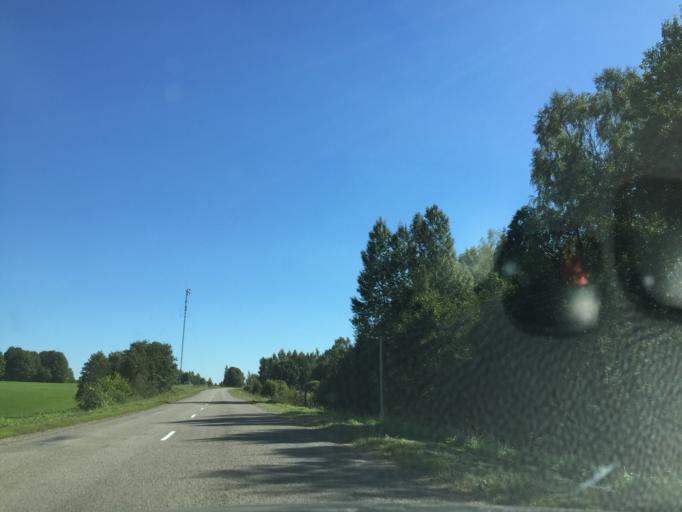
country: LV
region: Akniste
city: Akniste
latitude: 56.0552
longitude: 25.9020
